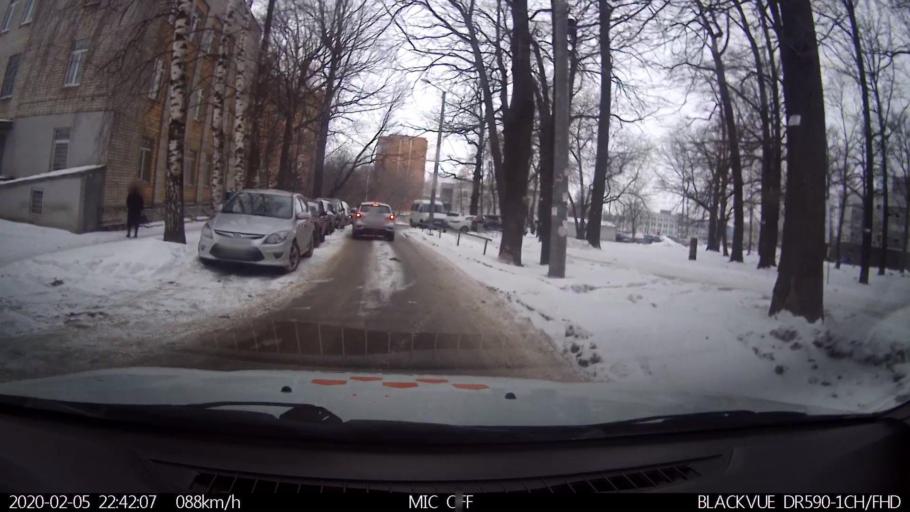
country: RU
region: Nizjnij Novgorod
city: Imeni Stepana Razina
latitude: 54.7188
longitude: 44.3501
